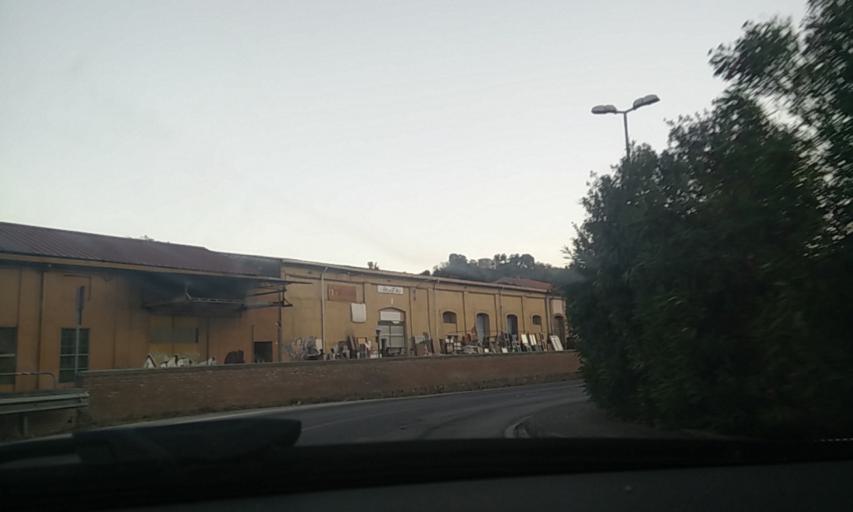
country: IT
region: Tuscany
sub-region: Provincia di Massa-Carrara
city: Carrara
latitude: 44.0748
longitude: 10.0929
